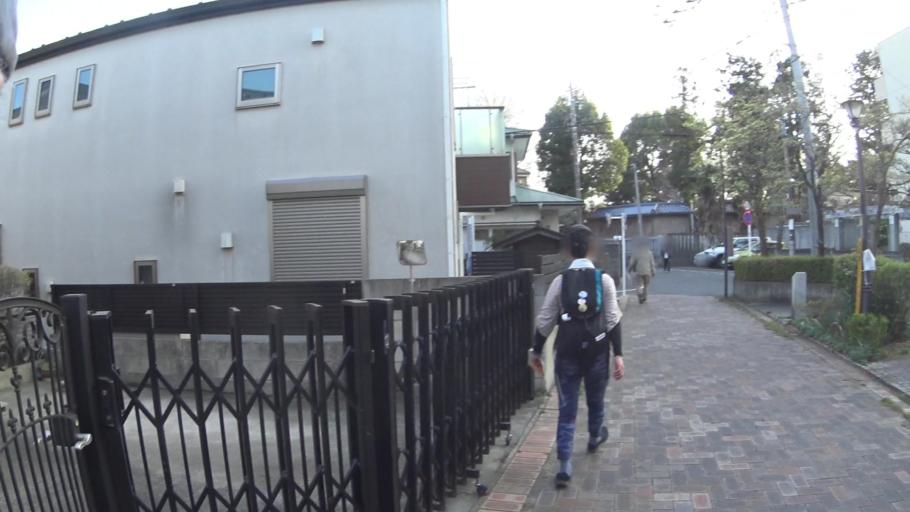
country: JP
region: Tokyo
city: Kokubunji
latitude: 35.7066
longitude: 139.5025
